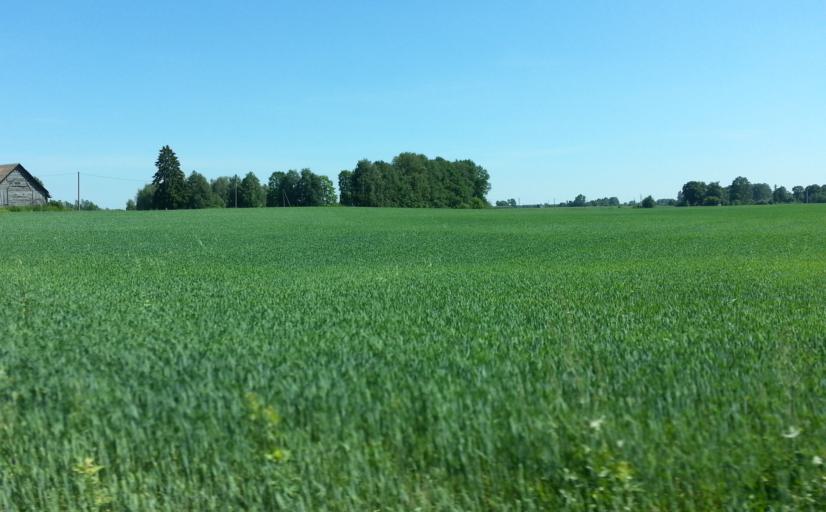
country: LT
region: Panevezys
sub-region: Birzai
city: Birzai
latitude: 56.2142
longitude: 24.6981
